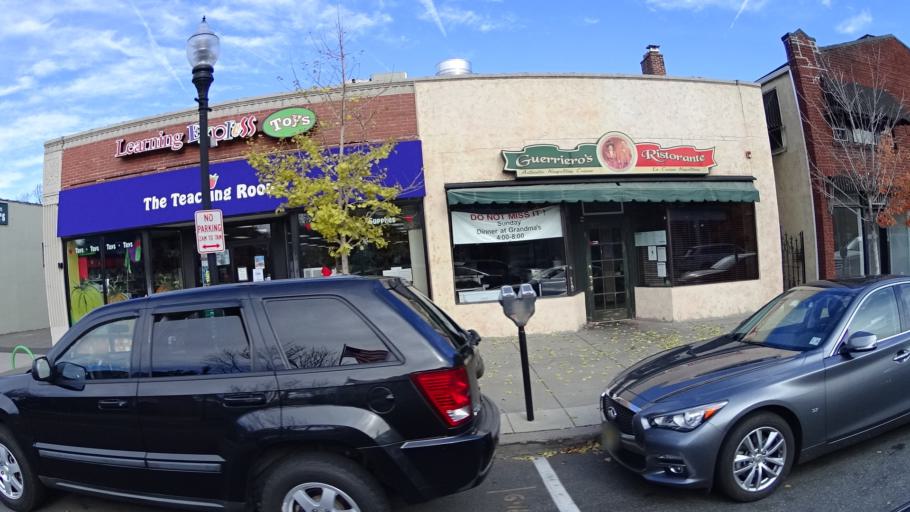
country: US
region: New Jersey
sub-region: Morris County
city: Morristown
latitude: 40.7925
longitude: -74.4766
